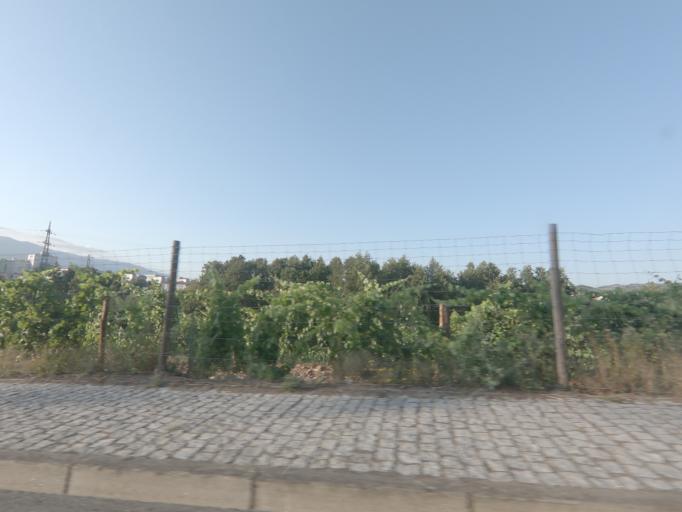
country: PT
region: Vila Real
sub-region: Vila Real
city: Vila Real
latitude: 41.2907
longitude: -7.7343
